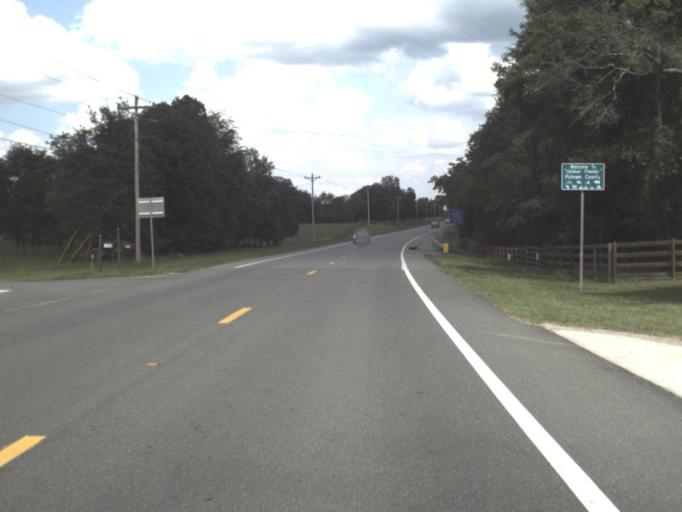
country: US
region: Florida
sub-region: Clay County
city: Keystone Heights
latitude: 29.7458
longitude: -81.9829
